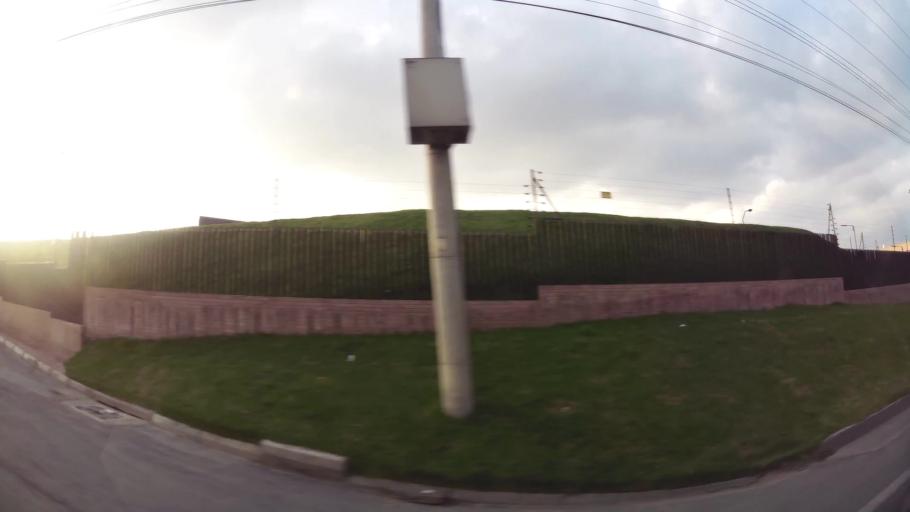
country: CO
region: Cundinamarca
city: Cota
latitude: 4.8042
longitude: -74.0942
